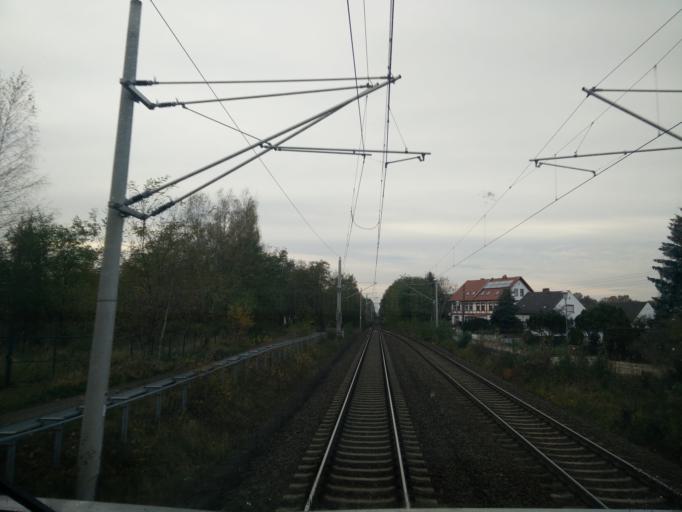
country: DE
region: Brandenburg
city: Vetschau
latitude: 51.7913
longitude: 14.0764
